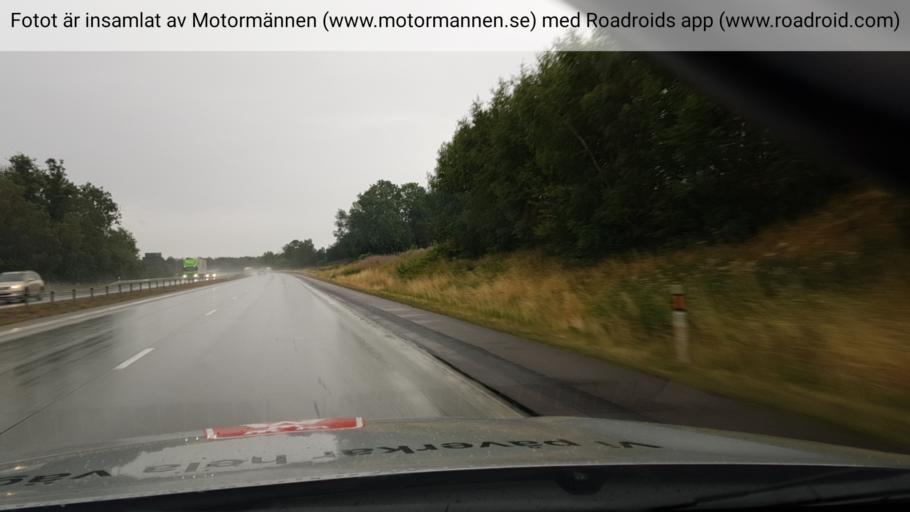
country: SE
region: Halland
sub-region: Halmstads Kommun
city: Getinge
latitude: 56.8270
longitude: 12.7100
